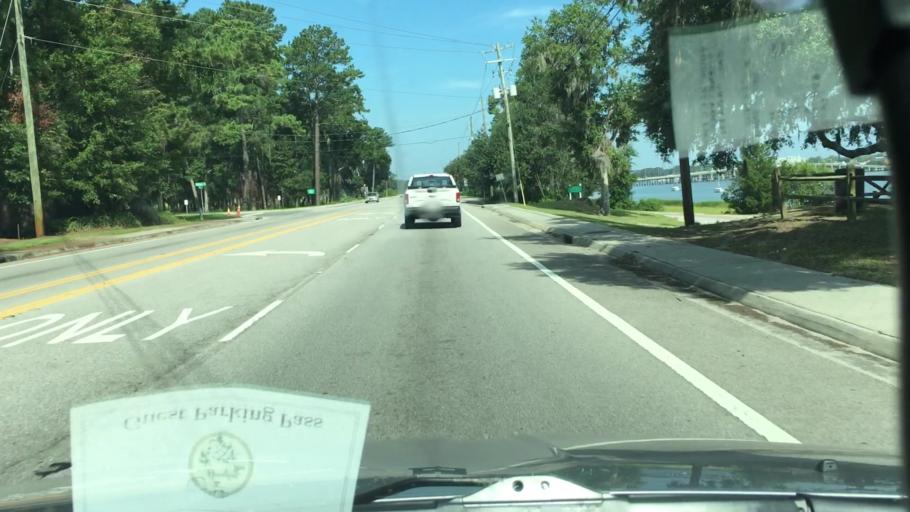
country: US
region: South Carolina
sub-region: Beaufort County
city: Beaufort
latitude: 32.4199
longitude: -80.6623
